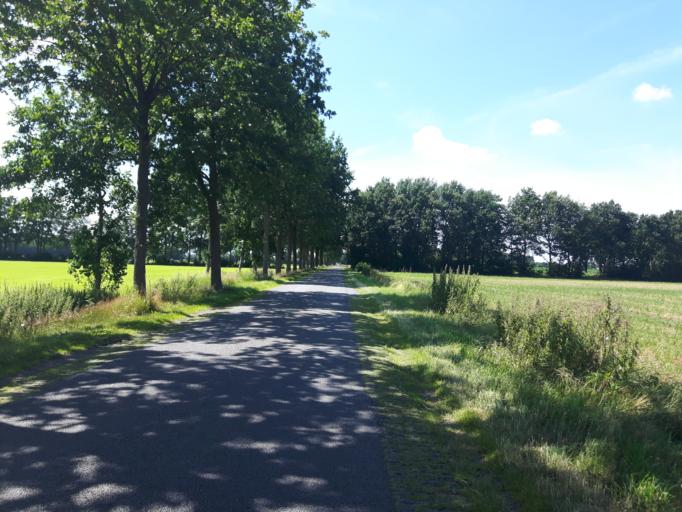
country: NL
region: Overijssel
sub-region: Gemeente Haaksbergen
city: Haaksbergen
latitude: 52.1816
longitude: 6.7552
